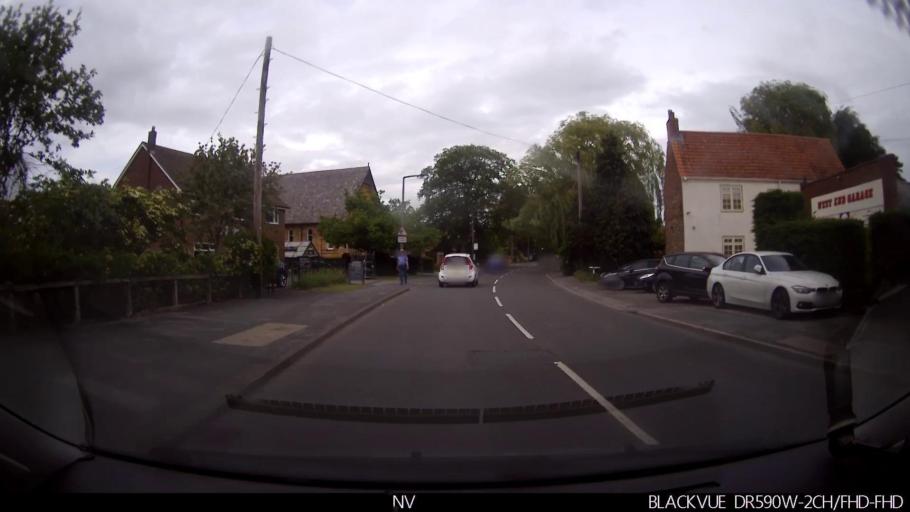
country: GB
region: England
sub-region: City of York
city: Wigginton
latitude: 54.0179
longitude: -1.0803
